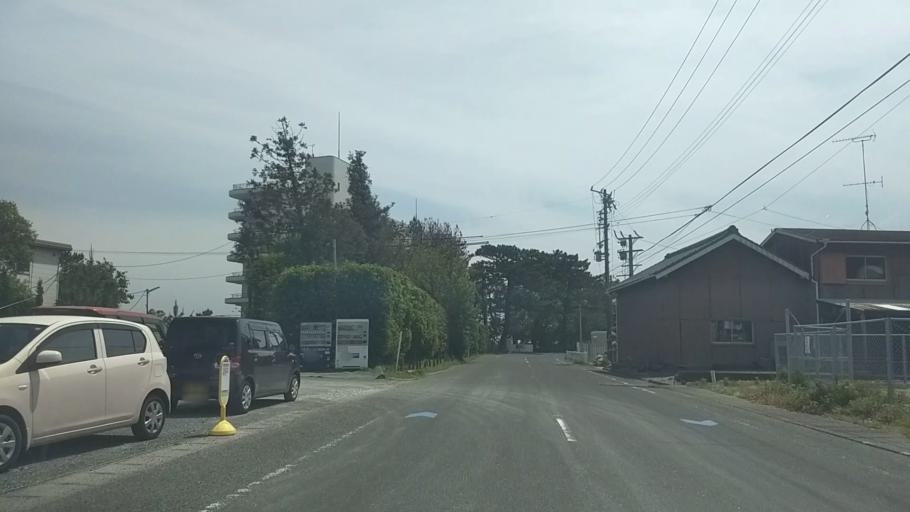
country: JP
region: Shizuoka
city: Kosai-shi
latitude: 34.7877
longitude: 137.5967
